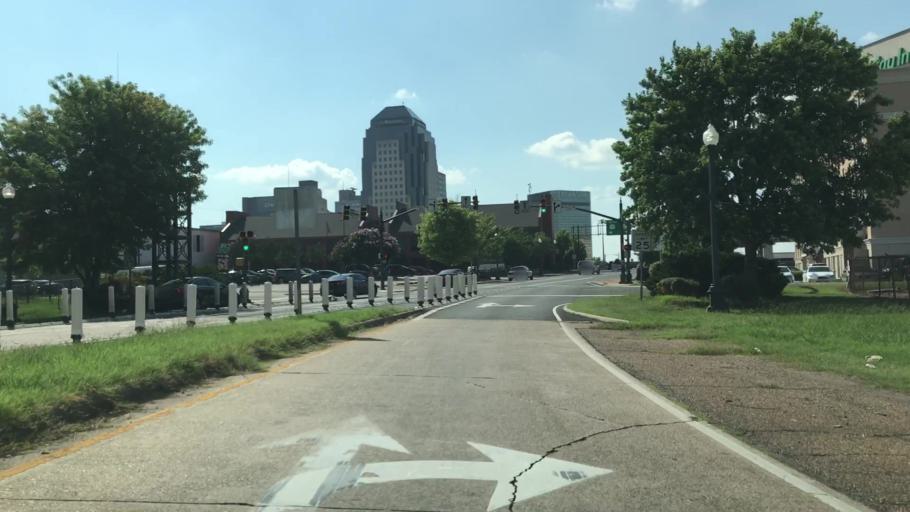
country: US
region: Louisiana
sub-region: Bossier Parish
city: Bossier City
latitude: 32.5115
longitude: -93.7430
